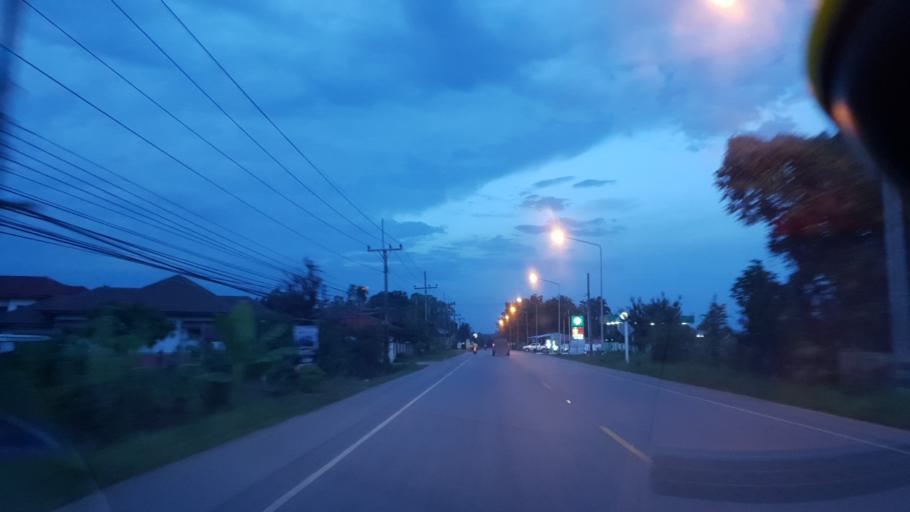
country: TH
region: Chiang Rai
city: Wiang Chiang Rung
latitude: 19.9805
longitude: 100.0240
